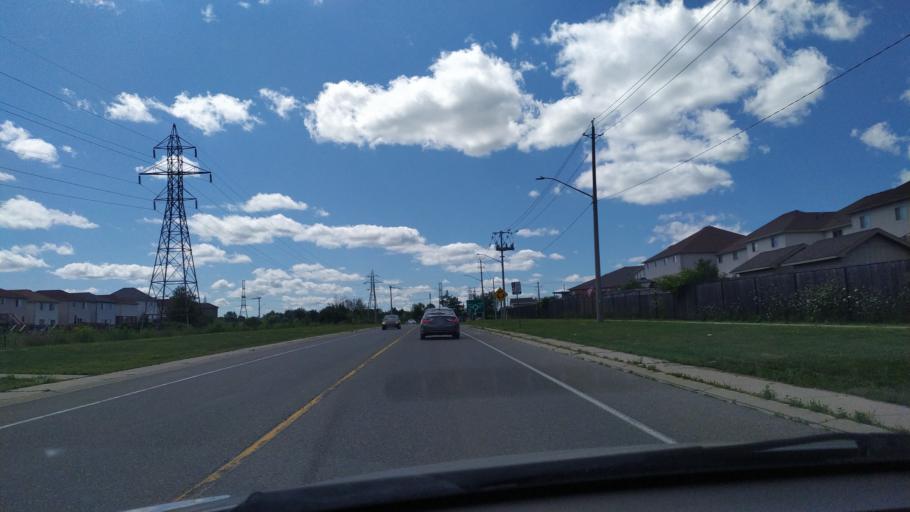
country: CA
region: Ontario
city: Kitchener
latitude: 43.4296
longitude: -80.5505
